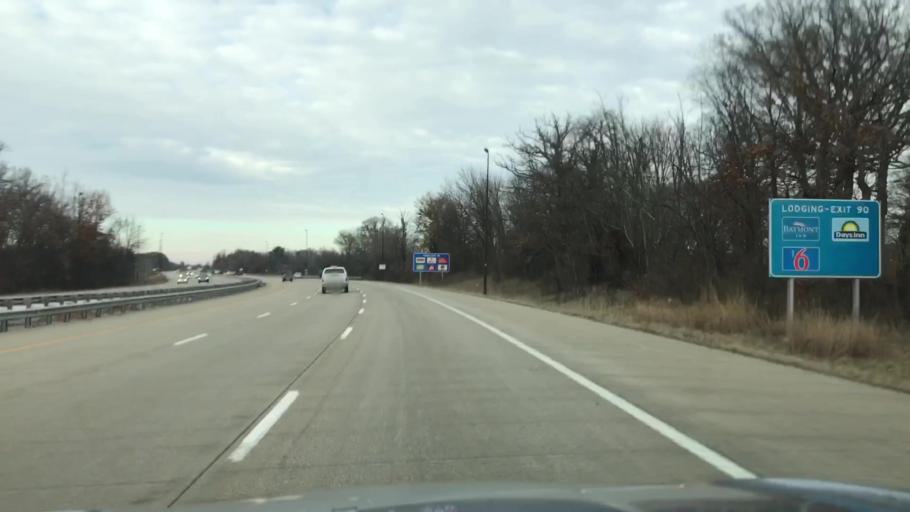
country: US
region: Illinois
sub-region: Sangamon County
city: Chatham
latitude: 39.6927
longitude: -89.6421
